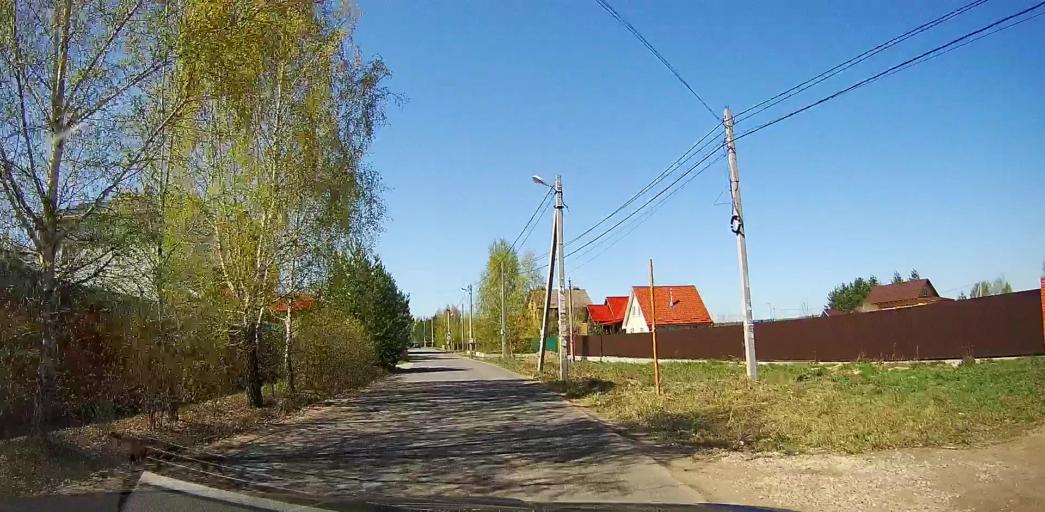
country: RU
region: Moskovskaya
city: Malyshevo
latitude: 55.4602
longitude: 38.3662
